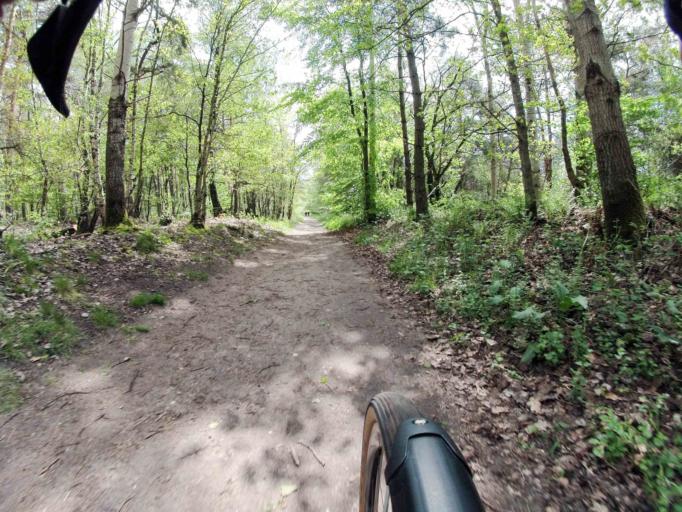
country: DE
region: North Rhine-Westphalia
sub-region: Regierungsbezirk Munster
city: Westerkappeln
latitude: 52.3341
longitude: 7.9175
